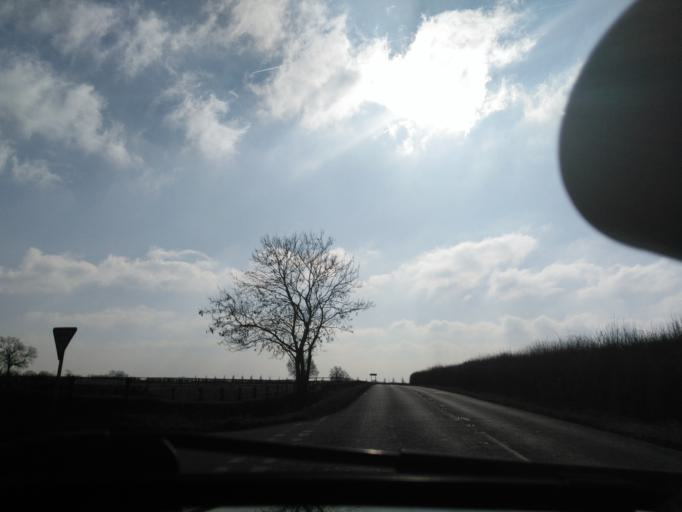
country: GB
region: England
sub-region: Wiltshire
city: Hankerton
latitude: 51.6266
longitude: -2.0754
